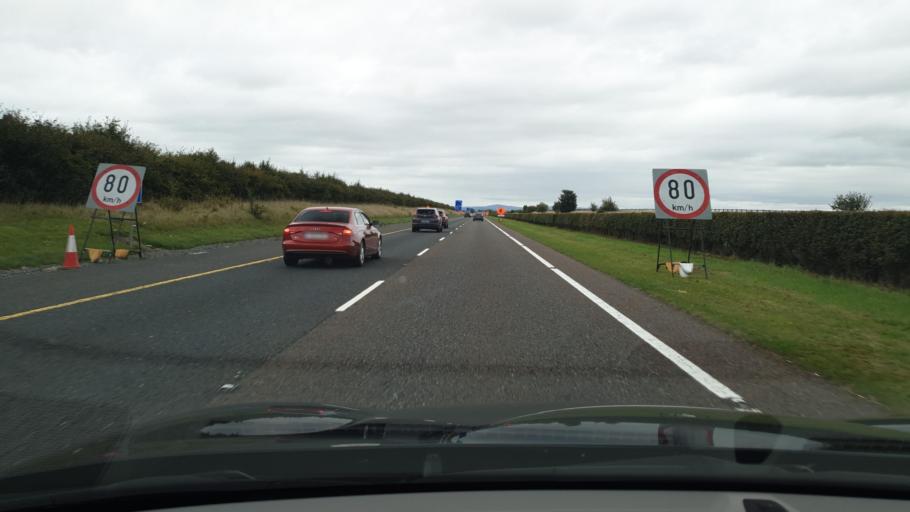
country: IE
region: Leinster
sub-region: Kildare
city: Athgarvan
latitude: 53.1583
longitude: -6.8511
